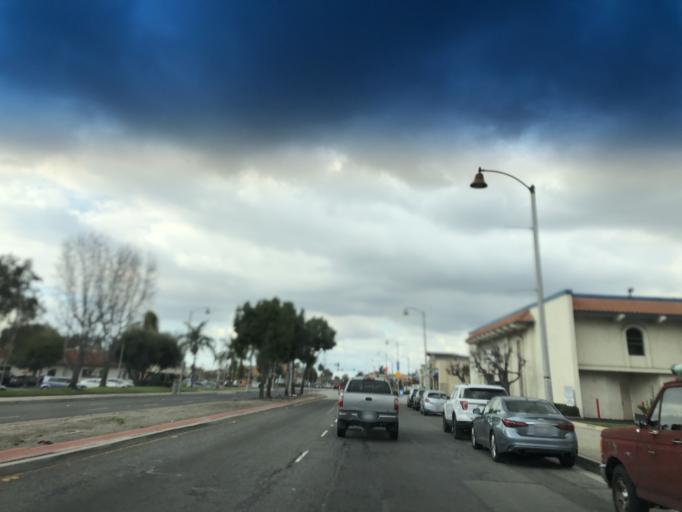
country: US
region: California
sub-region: Los Angeles County
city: Pico Rivera
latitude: 34.0005
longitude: -118.0817
